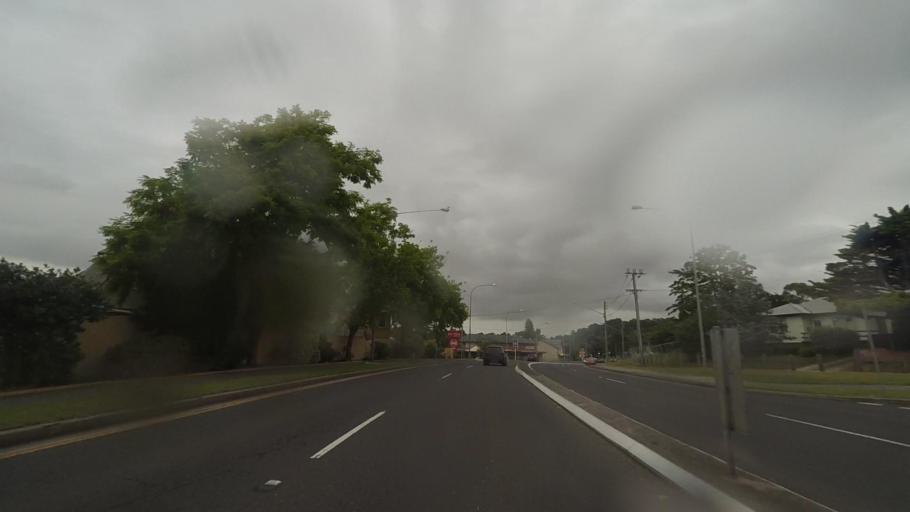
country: AU
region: New South Wales
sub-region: Wollongong
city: Mangerton
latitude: -34.4377
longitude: 150.8598
